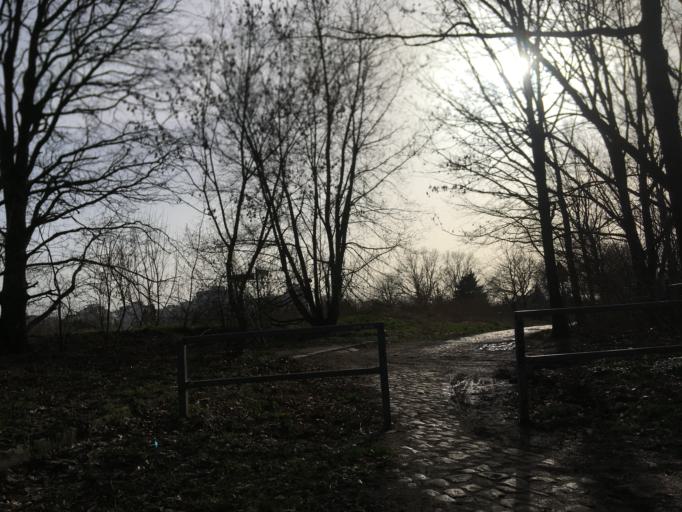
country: DE
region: Berlin
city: Lubars
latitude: 52.6112
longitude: 13.3522
